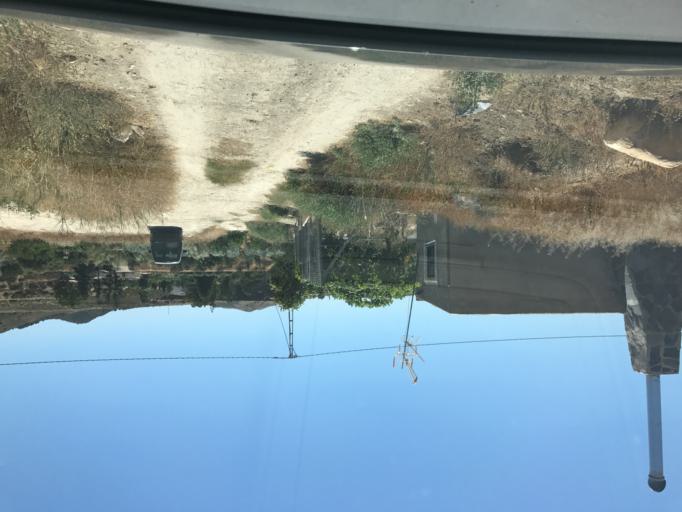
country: ES
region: Andalusia
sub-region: Provincia de Almeria
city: Fines
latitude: 37.3560
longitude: -2.2511
